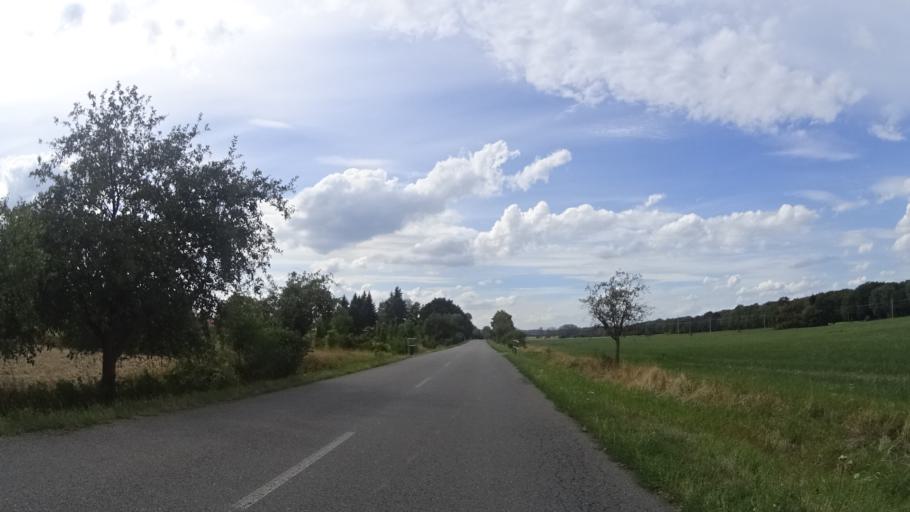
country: CZ
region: Olomoucky
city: Litovel
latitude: 49.7117
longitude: 17.0637
